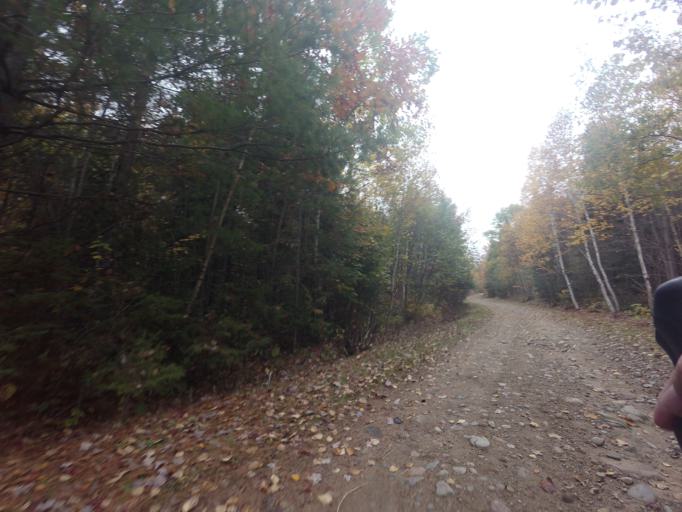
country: CA
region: Ontario
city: Petawawa
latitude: 45.7626
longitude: -77.3682
